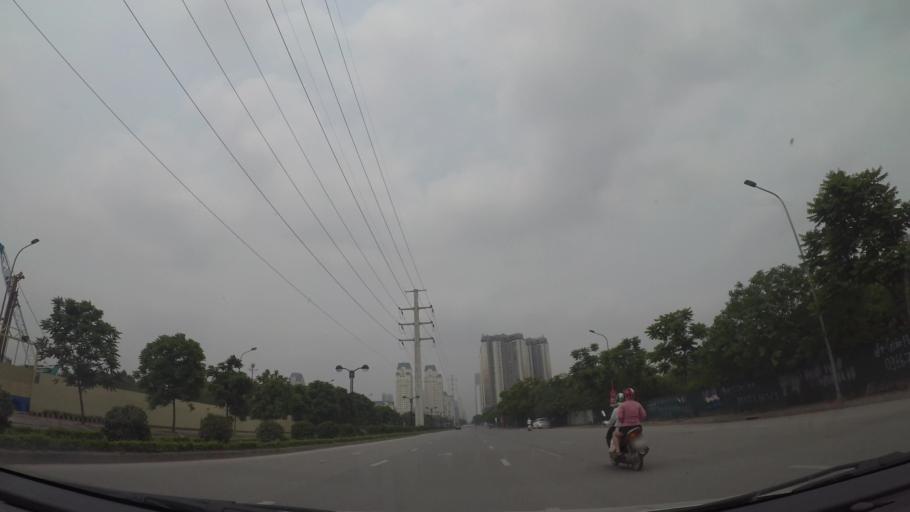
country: VN
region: Ha Noi
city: Cau Dien
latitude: 21.0087
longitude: 105.7699
